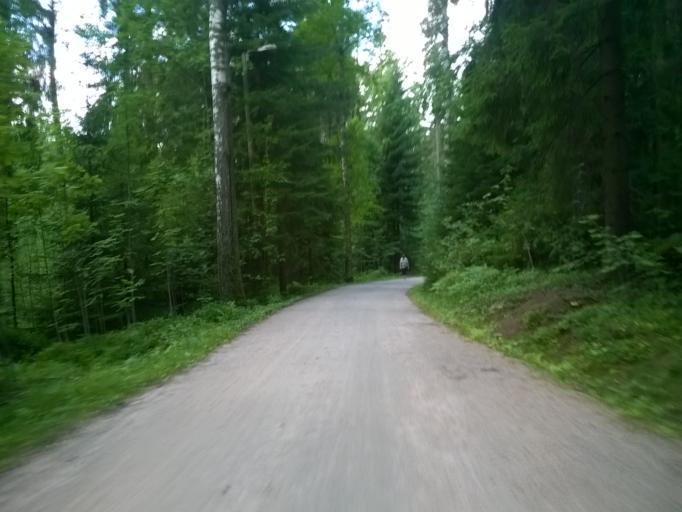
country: FI
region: Uusimaa
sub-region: Helsinki
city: Helsinki
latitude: 60.2618
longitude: 24.9079
